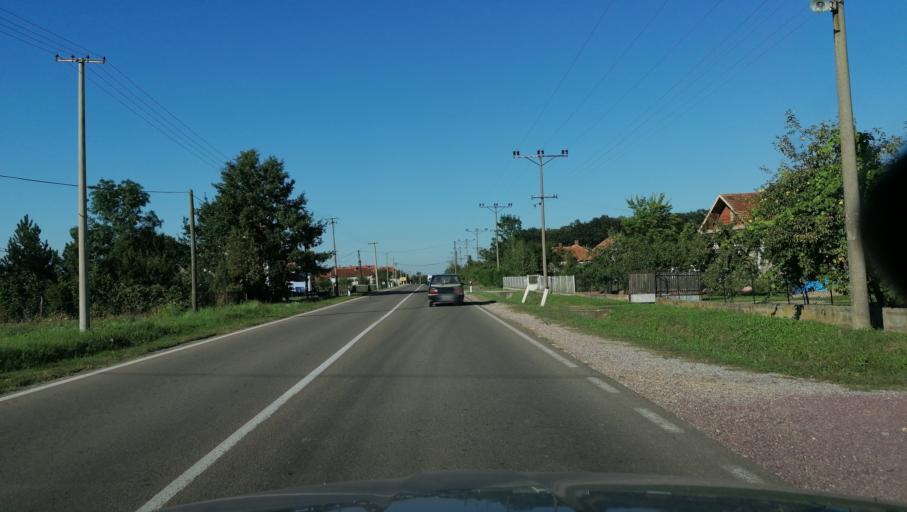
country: RS
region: Central Serbia
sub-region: Sumadijski Okrug
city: Knic
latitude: 43.9068
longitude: 20.6345
